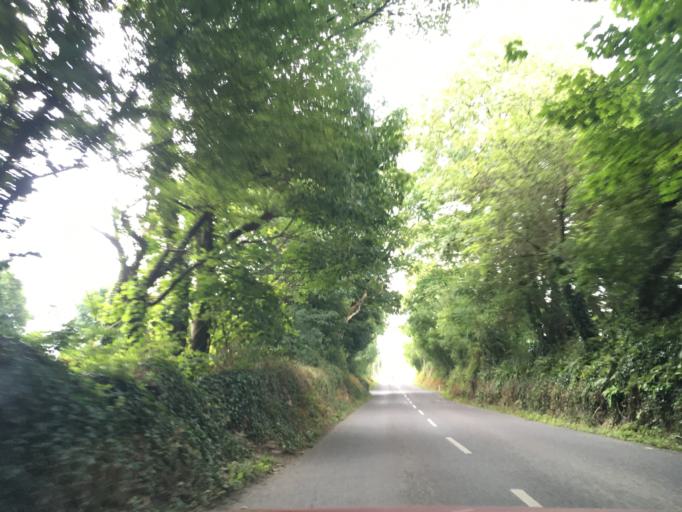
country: IE
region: Munster
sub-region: County Cork
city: Crosshaven
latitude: 51.7944
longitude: -8.2984
